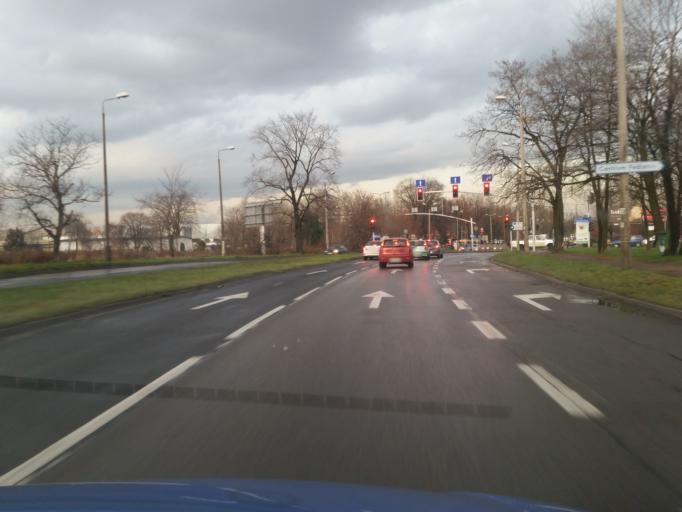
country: PL
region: Silesian Voivodeship
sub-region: Powiat bedzinski
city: Bedzin
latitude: 50.2784
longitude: 19.1746
